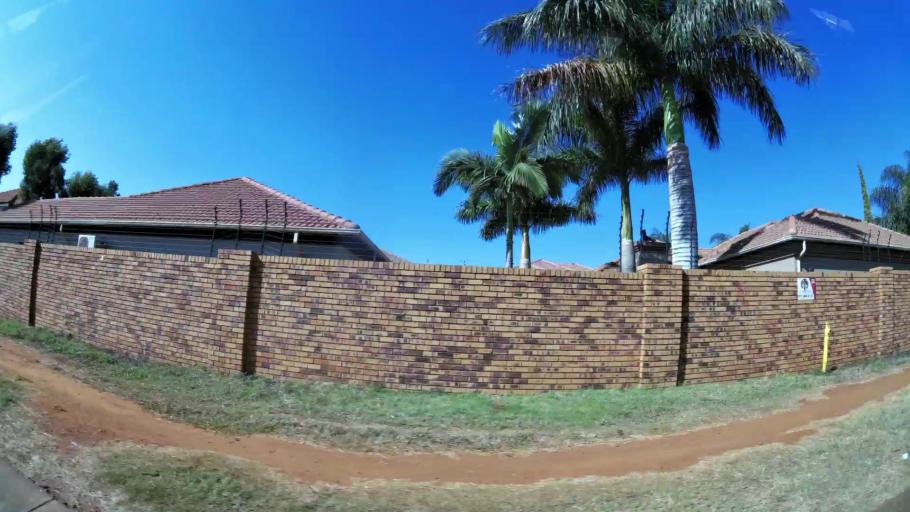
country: ZA
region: Gauteng
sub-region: City of Tshwane Metropolitan Municipality
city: Pretoria
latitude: -25.6635
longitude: 28.2558
